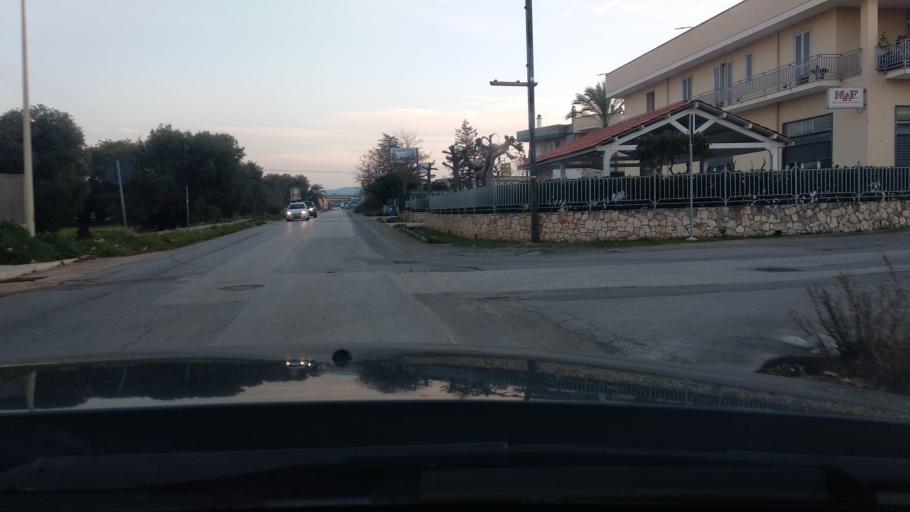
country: IT
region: Apulia
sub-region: Provincia di Brindisi
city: Fasano
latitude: 40.8504
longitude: 17.3538
